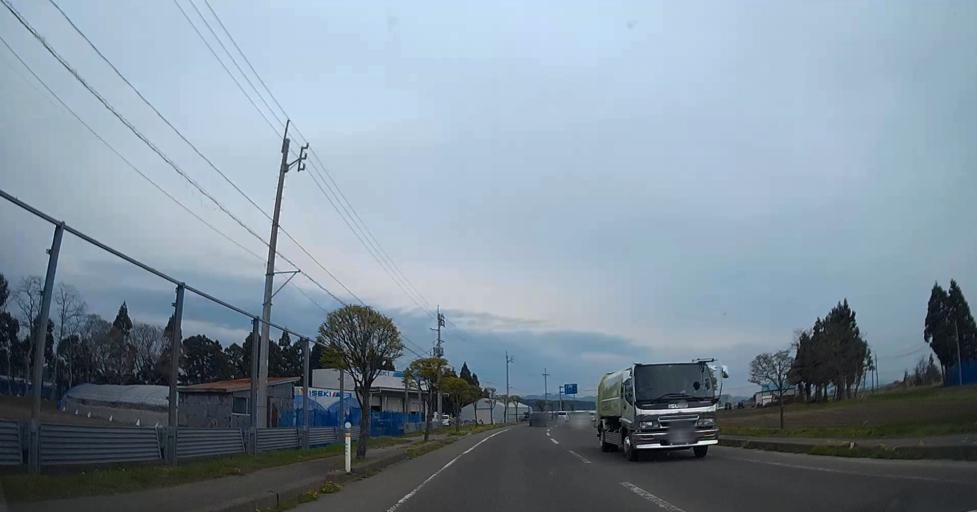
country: JP
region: Aomori
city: Aomori Shi
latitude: 40.8690
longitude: 140.6765
